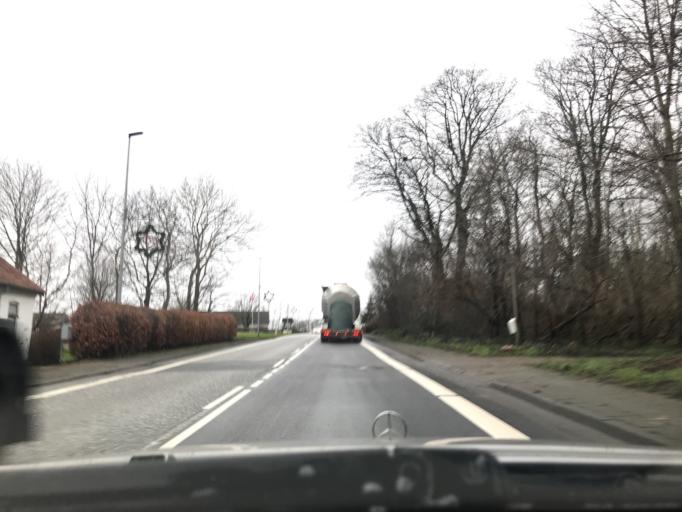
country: DK
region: South Denmark
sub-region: Haderslev Kommune
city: Gram
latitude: 55.2286
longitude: 8.9912
